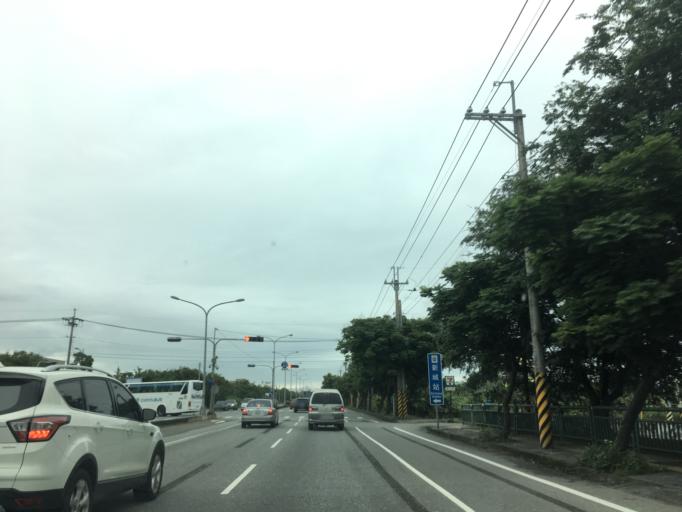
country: TW
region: Taiwan
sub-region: Hualien
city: Hualian
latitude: 24.1192
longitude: 121.6424
